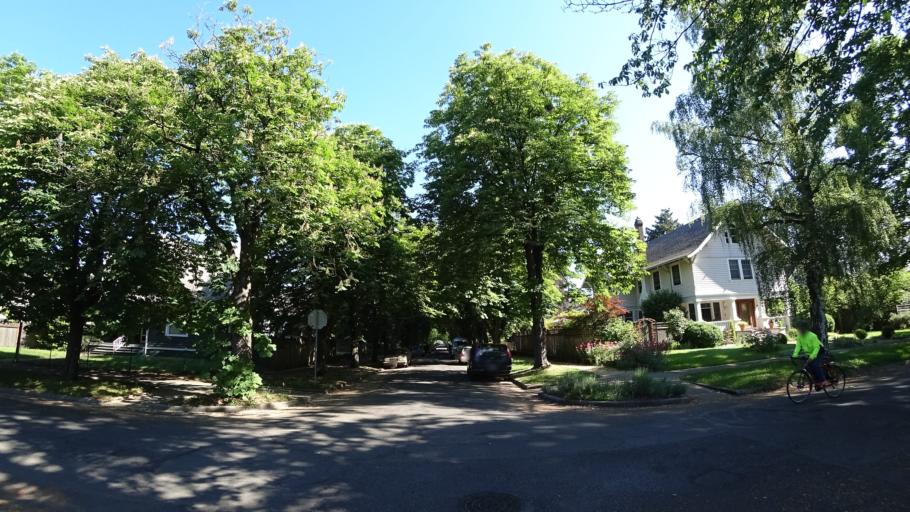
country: US
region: Oregon
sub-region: Multnomah County
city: Portland
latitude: 45.5638
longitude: -122.6648
